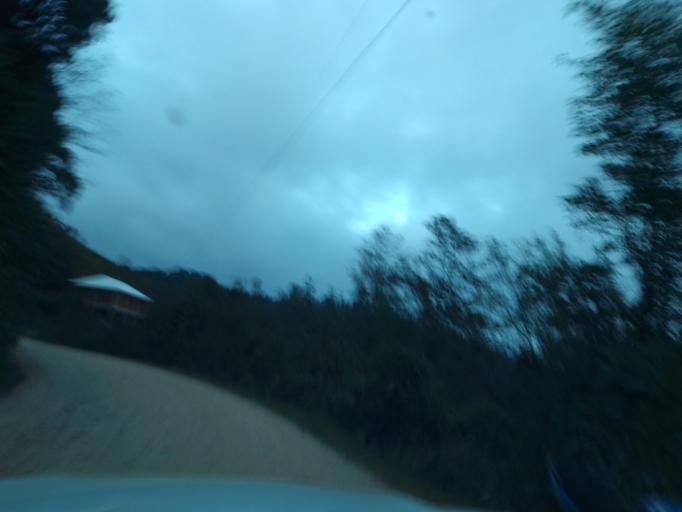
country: MX
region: Chiapas
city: Motozintla de Mendoza
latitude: 15.2209
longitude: -92.2358
